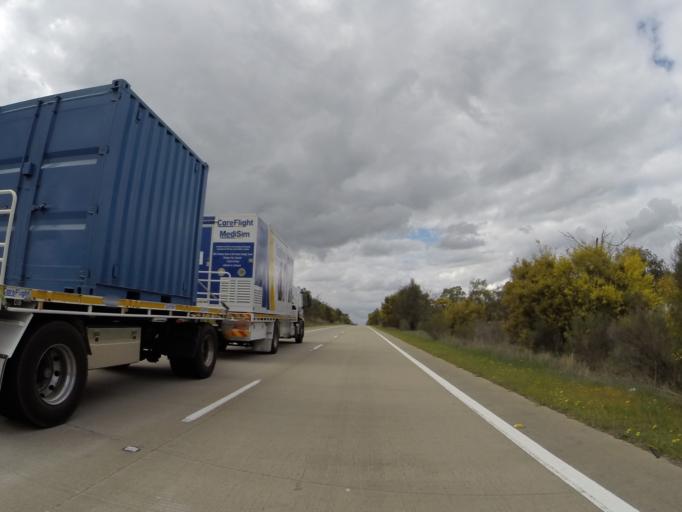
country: AU
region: New South Wales
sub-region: Goulburn Mulwaree
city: Goulburn
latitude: -34.8084
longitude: 149.4864
